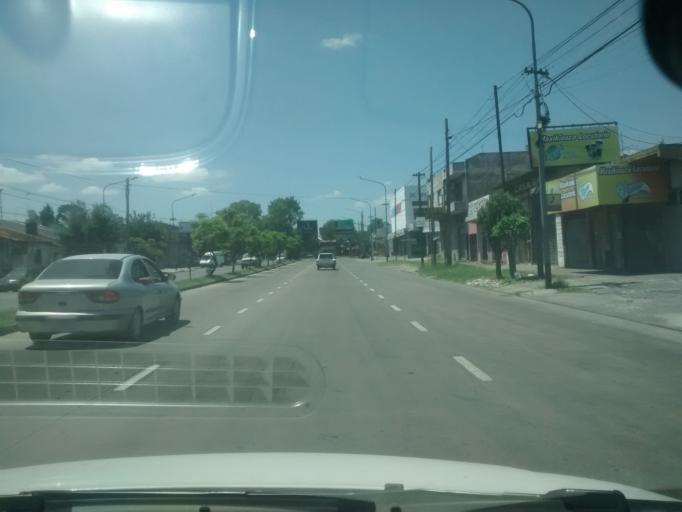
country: AR
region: Buenos Aires
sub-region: Partido de Moron
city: Moron
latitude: -34.6604
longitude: -58.6095
